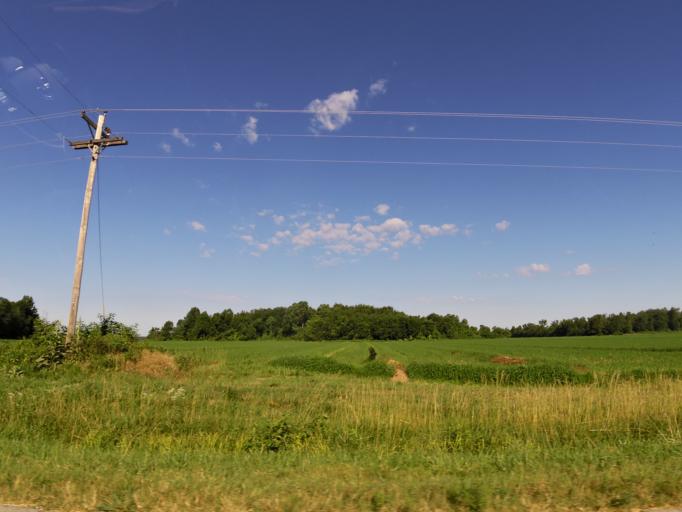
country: US
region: Arkansas
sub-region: Clay County
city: Corning
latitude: 36.5785
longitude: -90.5207
